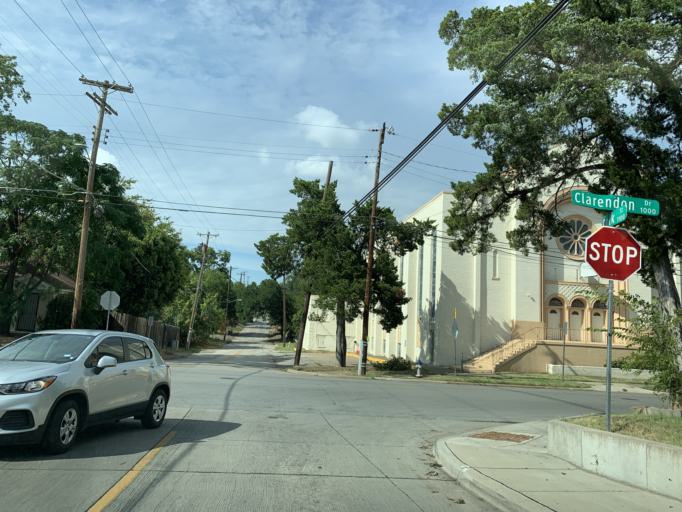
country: US
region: Texas
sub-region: Dallas County
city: Cockrell Hill
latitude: 32.7353
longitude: -96.8400
